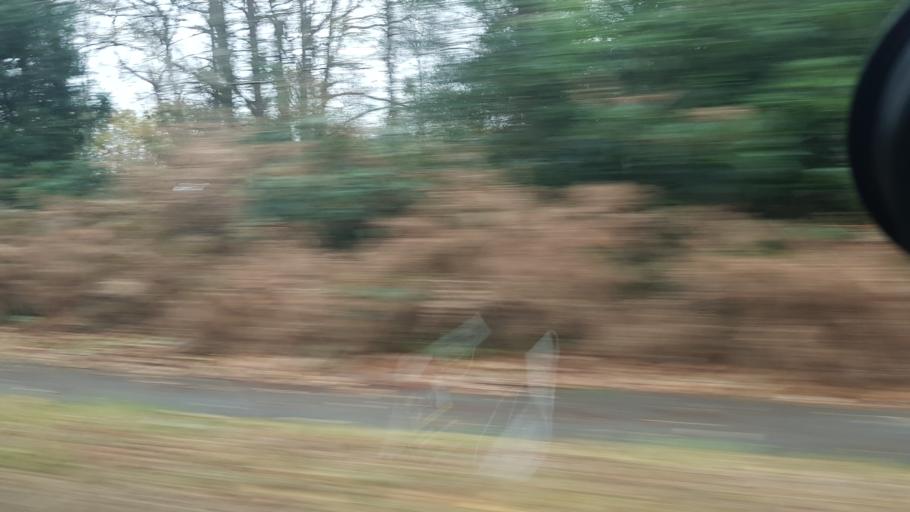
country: GB
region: England
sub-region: Hampshire
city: Fleet
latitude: 51.3119
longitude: -0.8129
